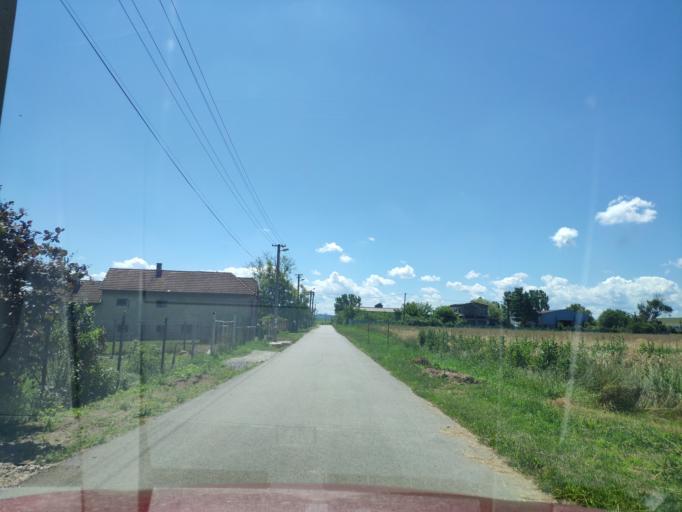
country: HU
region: Borsod-Abauj-Zemplen
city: Ozd
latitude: 48.3358
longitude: 20.2967
